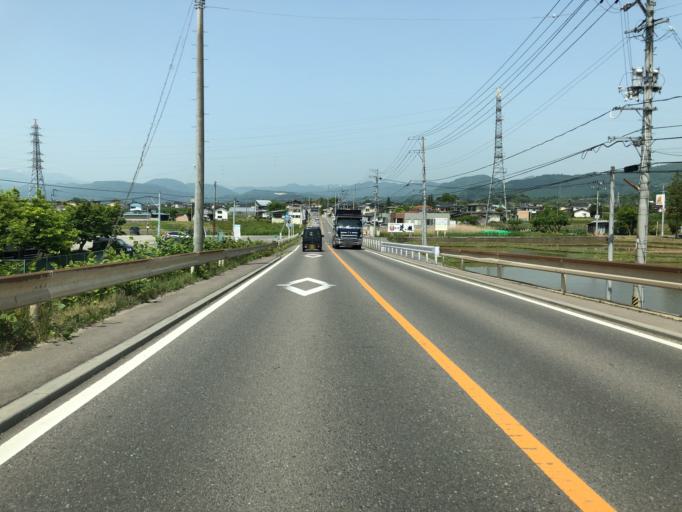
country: JP
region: Fukushima
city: Hobaramachi
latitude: 37.8226
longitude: 140.4909
